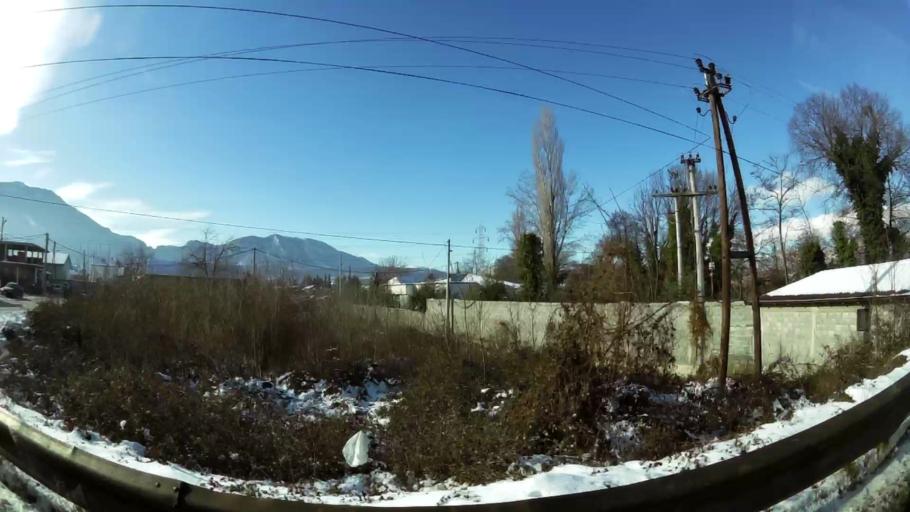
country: MK
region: Saraj
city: Saraj
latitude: 41.9950
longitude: 21.3274
